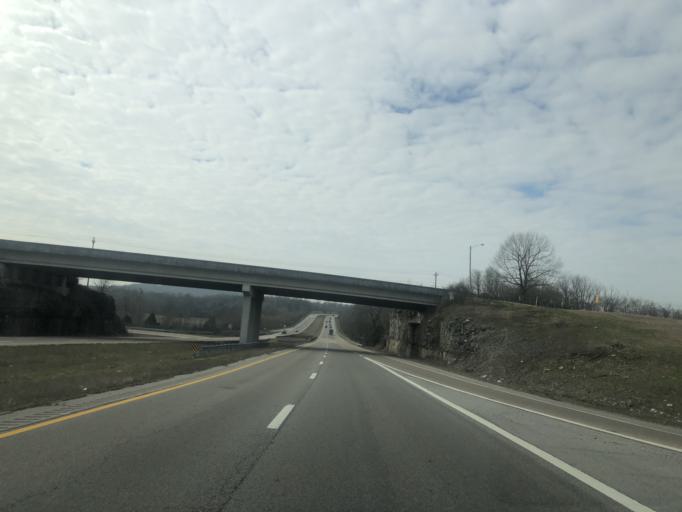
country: US
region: Tennessee
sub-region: Maury County
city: Columbia
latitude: 35.6302
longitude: -87.0662
